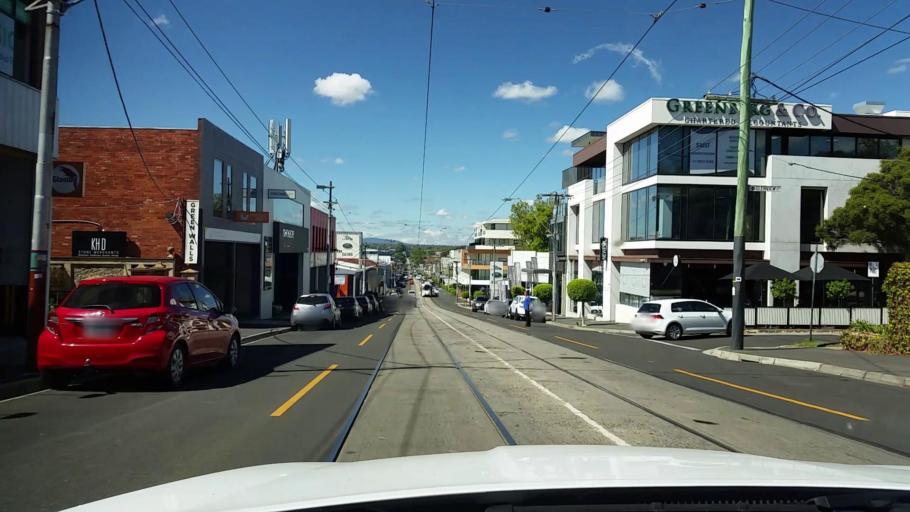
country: AU
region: Victoria
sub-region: Stonnington
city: Glen Iris
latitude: -37.8524
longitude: 145.0360
